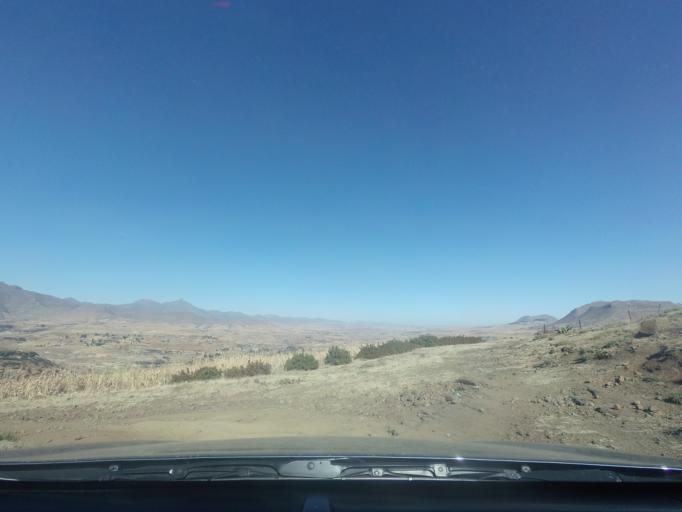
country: LS
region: Berea
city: Teyateyaneng
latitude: -29.2389
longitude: 27.8695
